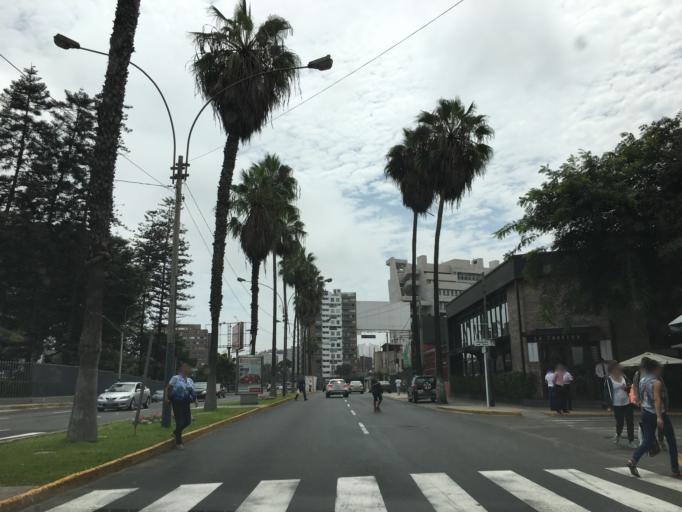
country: PE
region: Lima
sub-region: Lima
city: Surco
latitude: -12.1373
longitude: -77.0225
